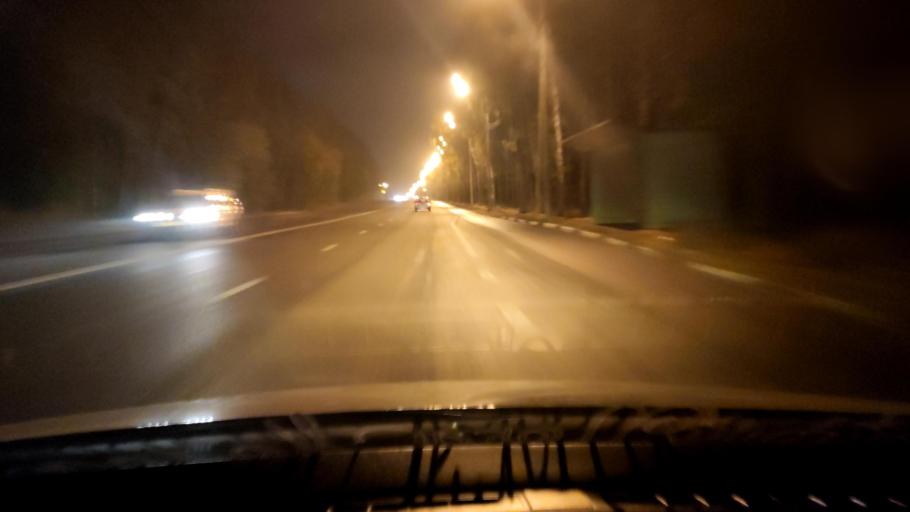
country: RU
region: Voronezj
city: Pridonskoy
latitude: 51.6915
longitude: 39.0982
